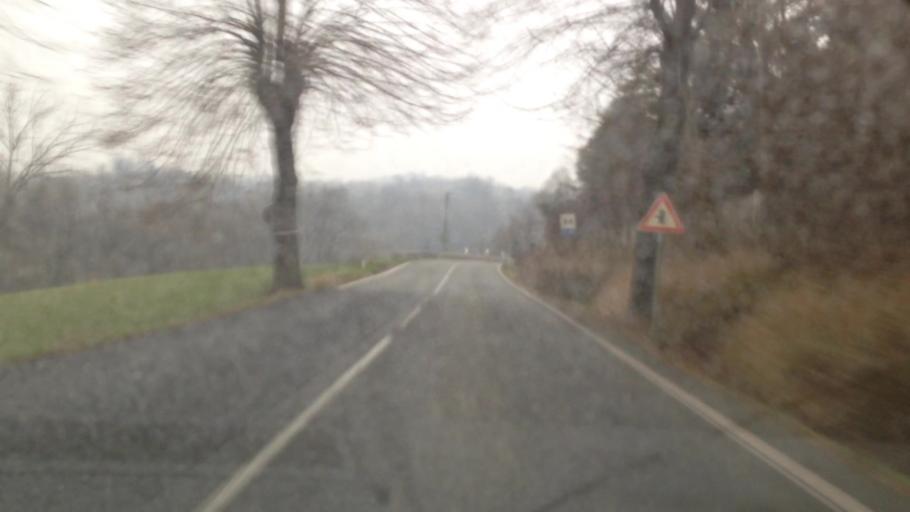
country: IT
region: Piedmont
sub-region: Provincia di Torino
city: Brozolo
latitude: 45.1307
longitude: 8.0582
